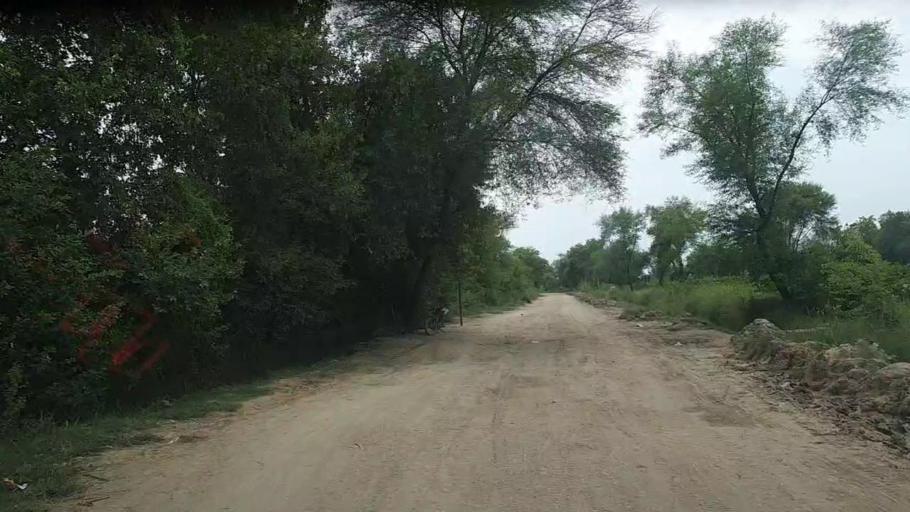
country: PK
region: Sindh
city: Bhiria
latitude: 26.8881
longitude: 68.2961
